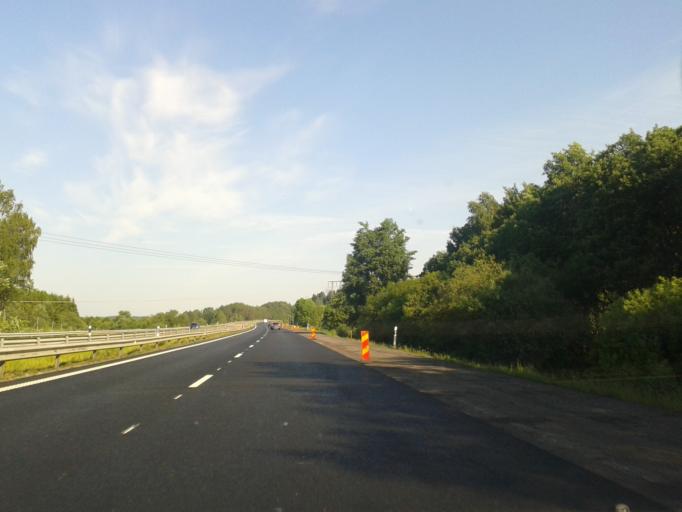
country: SE
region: Vaestra Goetaland
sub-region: Kungalvs Kommun
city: Kode
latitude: 57.9042
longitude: 11.9107
